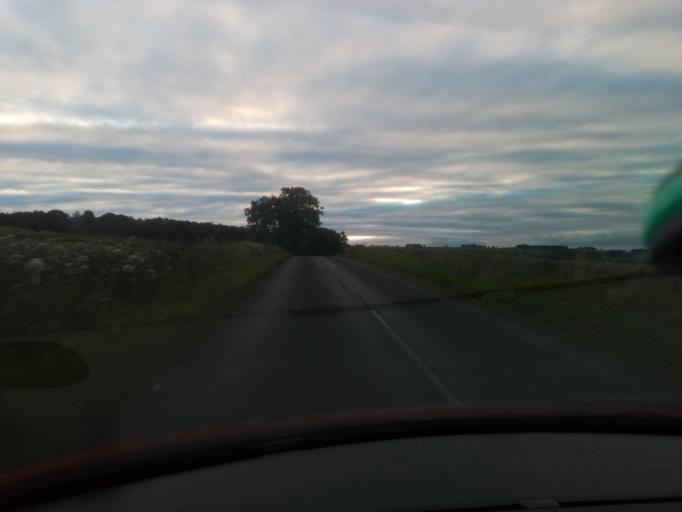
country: GB
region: England
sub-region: Northumberland
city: Bardon Mill
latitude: 54.9010
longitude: -2.2791
